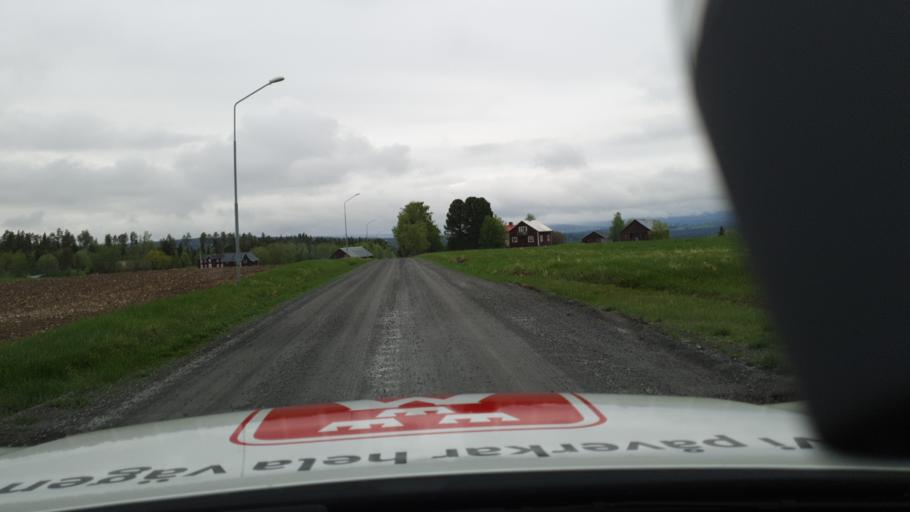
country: SE
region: Jaemtland
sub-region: Krokoms Kommun
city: Valla
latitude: 63.3142
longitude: 13.9740
